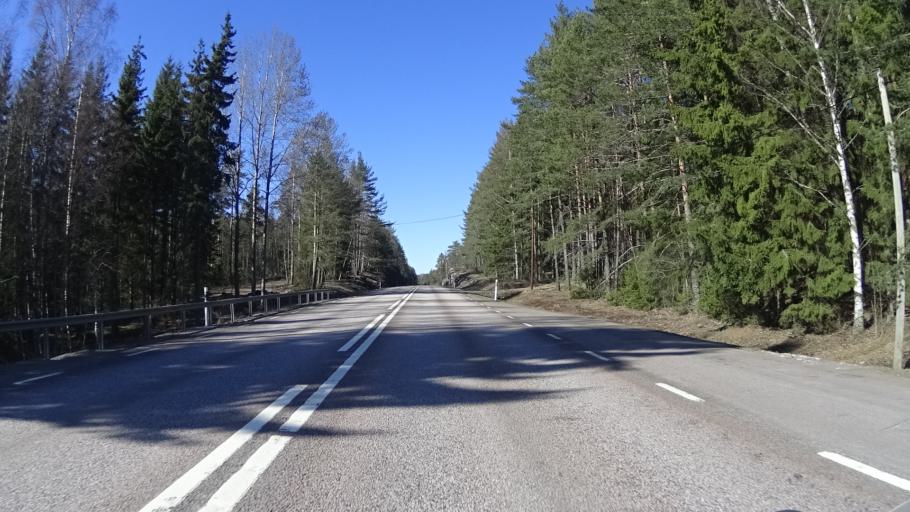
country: SE
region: Vaermland
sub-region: Karlstads Kommun
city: Edsvalla
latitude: 59.5872
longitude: 13.0126
